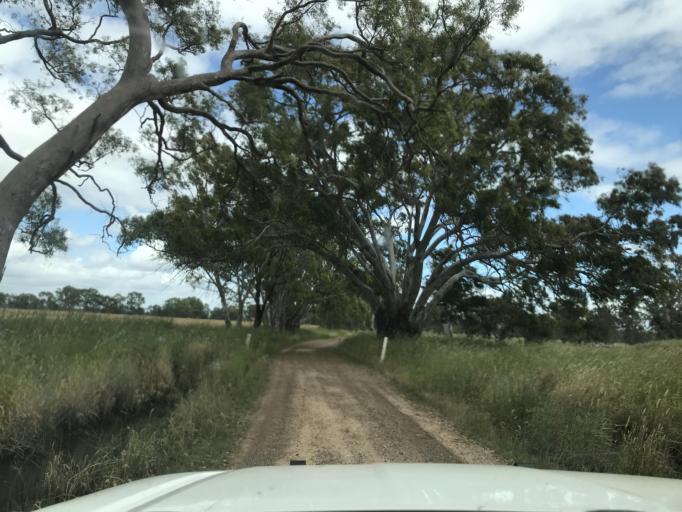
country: AU
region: South Australia
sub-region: Naracoorte and Lucindale
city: Naracoorte
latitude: -36.9000
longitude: 141.3970
